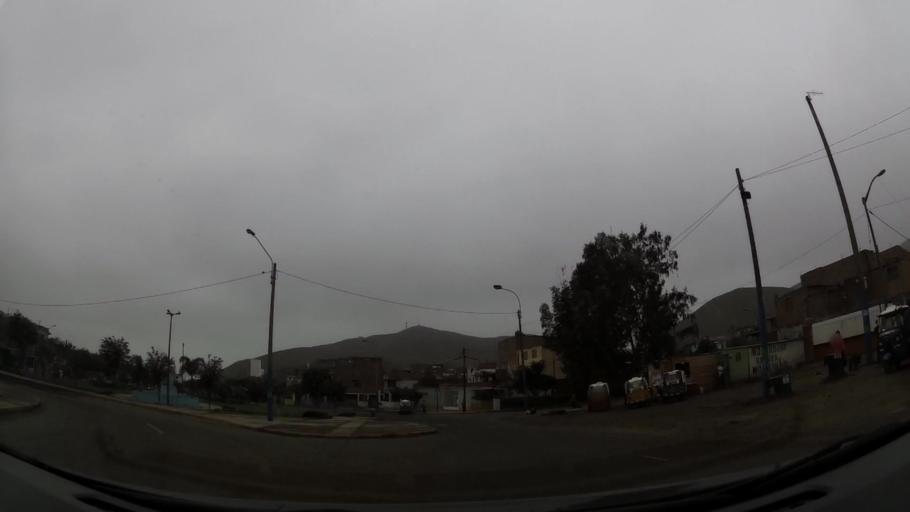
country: PE
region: Lima
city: Ventanilla
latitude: -11.8677
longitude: -77.1140
